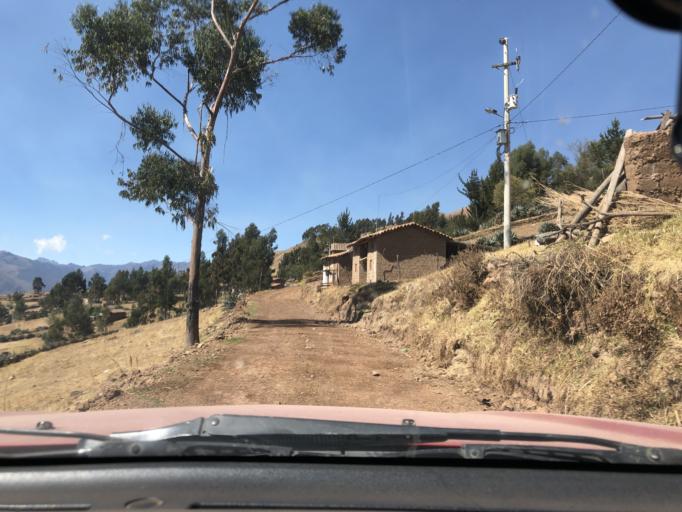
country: PE
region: Ayacucho
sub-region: Provincia de La Mar
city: Chilcas
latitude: -13.1690
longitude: -73.8544
